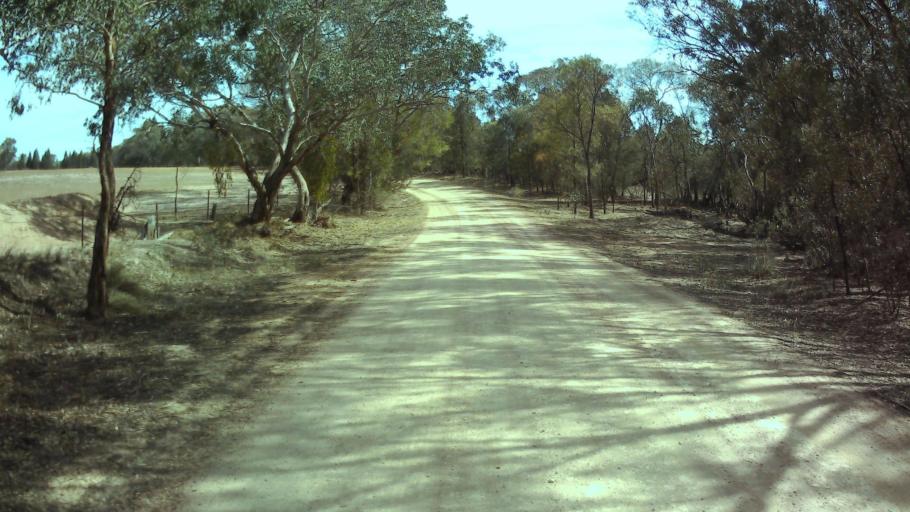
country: AU
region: New South Wales
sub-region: Weddin
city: Grenfell
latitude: -33.8824
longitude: 148.1511
